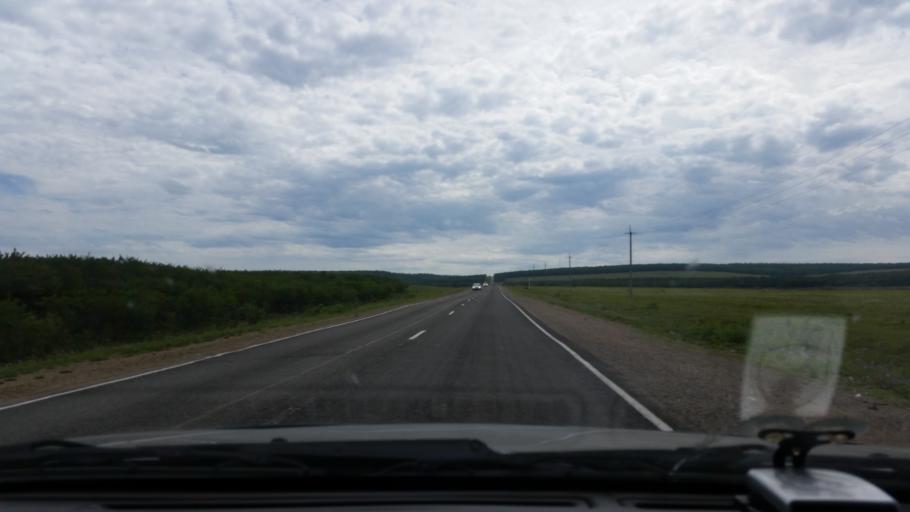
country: RU
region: Irkutsk
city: Bayanday
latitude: 53.0500
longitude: 105.5347
